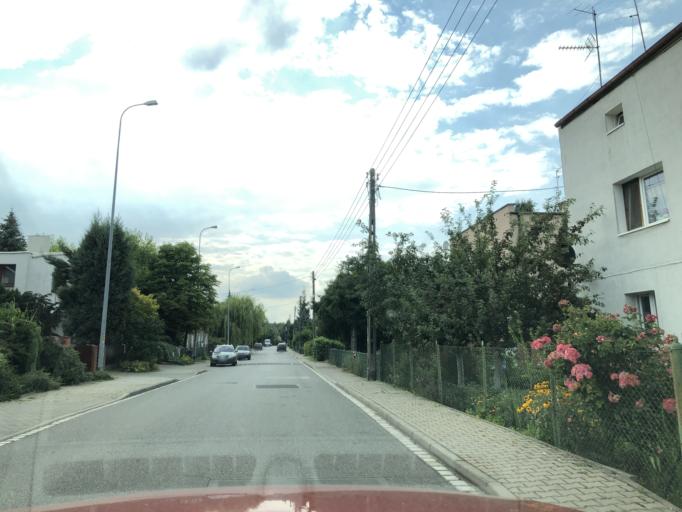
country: PL
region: Lower Silesian Voivodeship
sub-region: Powiat wroclawski
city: Smolec
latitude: 51.1574
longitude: 16.9007
